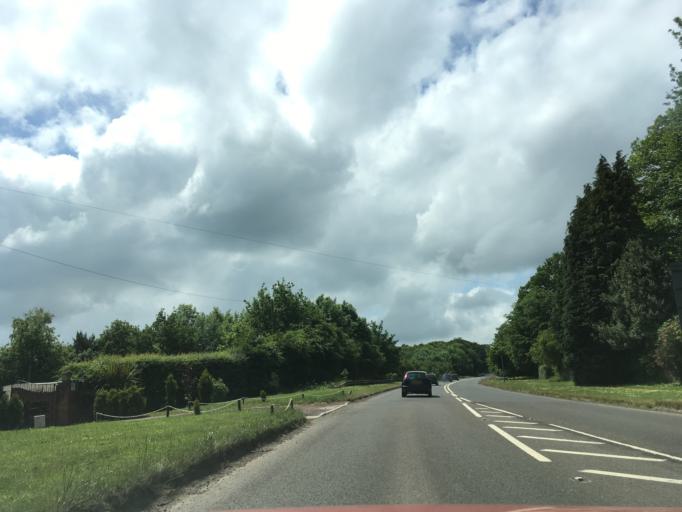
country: GB
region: England
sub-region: Devon
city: Uffculme
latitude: 50.9391
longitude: -3.3024
